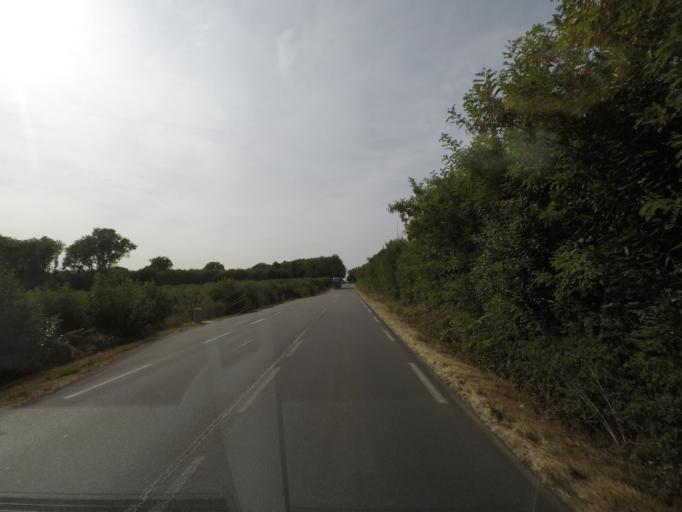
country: FR
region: Poitou-Charentes
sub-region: Departement des Deux-Sevres
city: Chef-Boutonne
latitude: 46.1836
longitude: -0.0339
